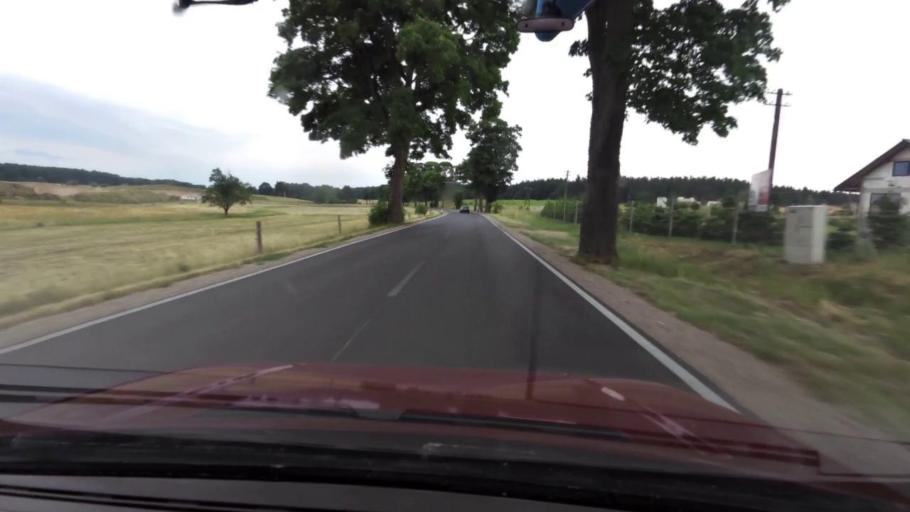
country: PL
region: West Pomeranian Voivodeship
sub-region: Powiat koszalinski
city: Sianow
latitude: 54.1671
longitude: 16.4344
